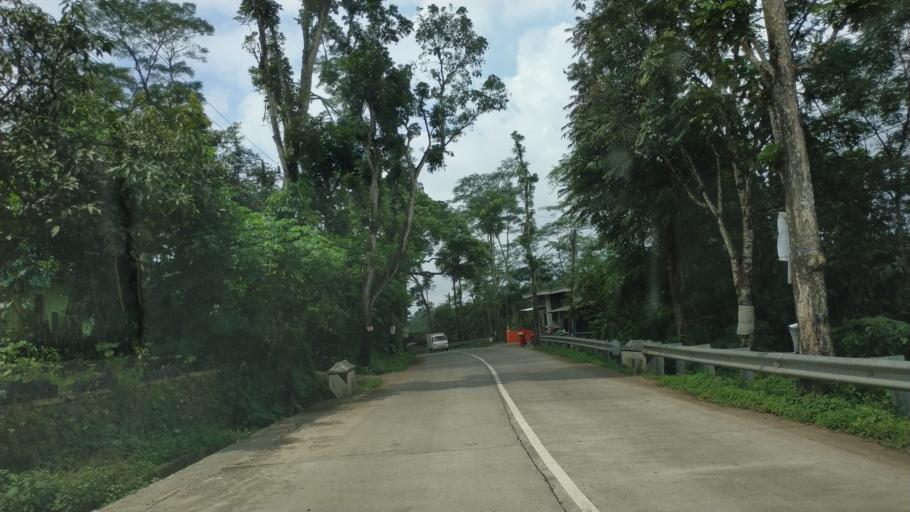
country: ID
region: Central Java
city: Weleri
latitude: -7.1044
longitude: 110.0722
